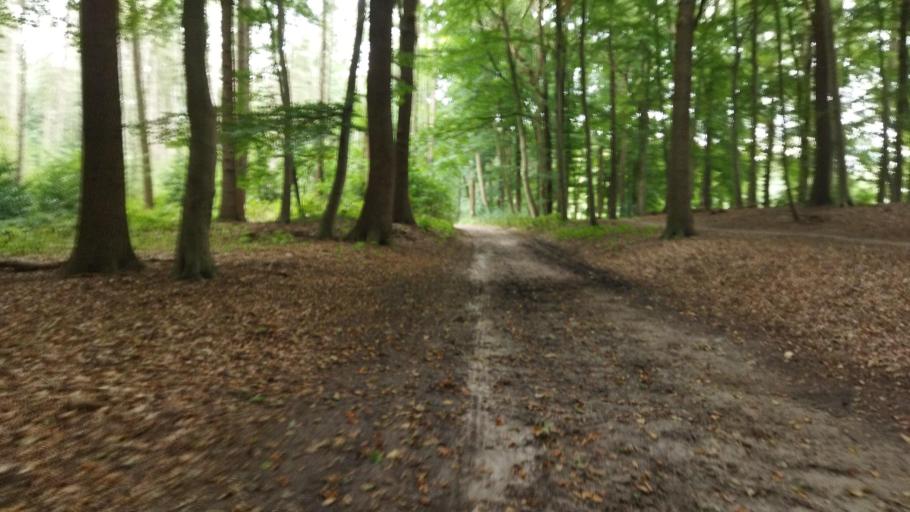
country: DE
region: North Rhine-Westphalia
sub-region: Regierungsbezirk Munster
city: Telgte
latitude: 52.0199
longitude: 7.7637
